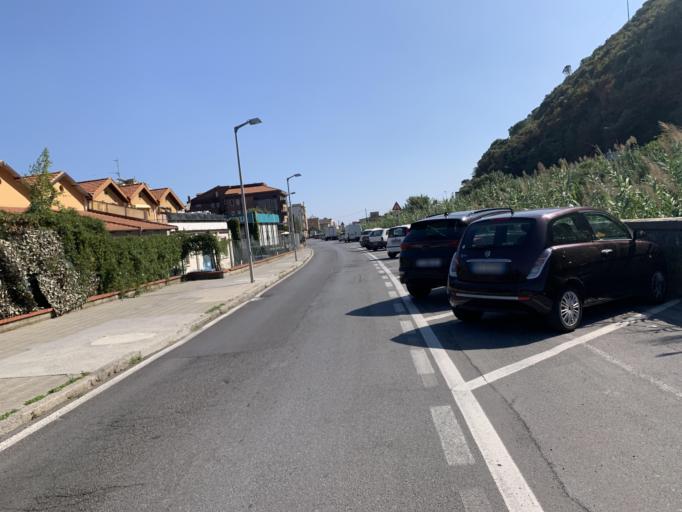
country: IT
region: Liguria
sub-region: Provincia di Savona
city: Finale Ligure
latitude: 44.1716
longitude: 8.3332
